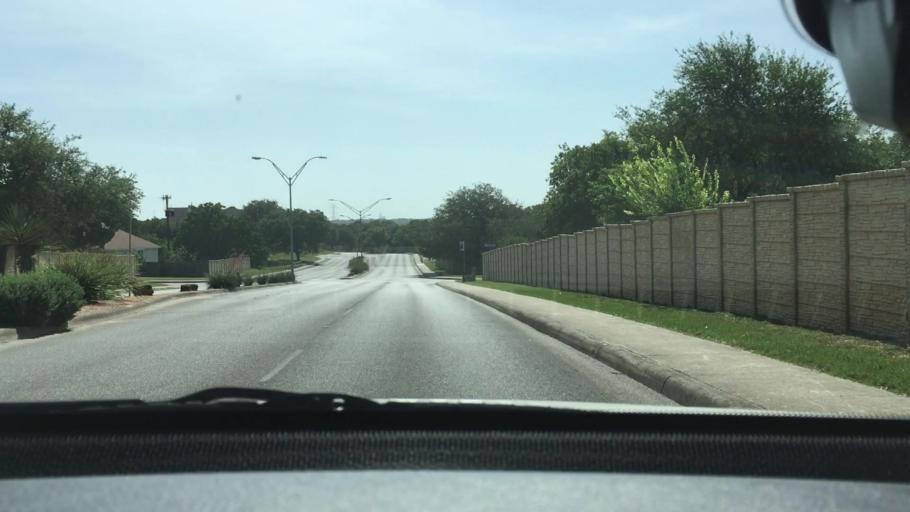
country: US
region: Texas
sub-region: Bexar County
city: Live Oak
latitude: 29.5878
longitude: -98.4034
